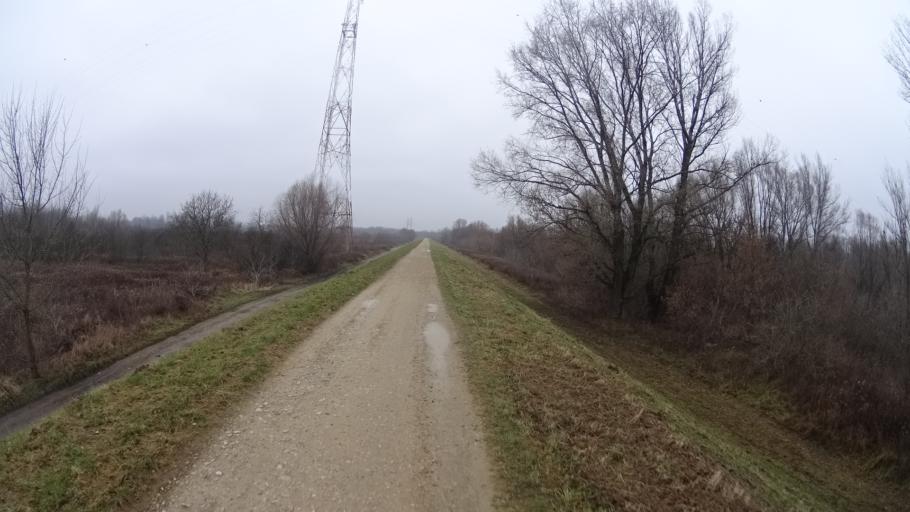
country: PL
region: Masovian Voivodeship
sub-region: Warszawa
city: Wilanow
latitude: 52.1974
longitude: 21.0998
